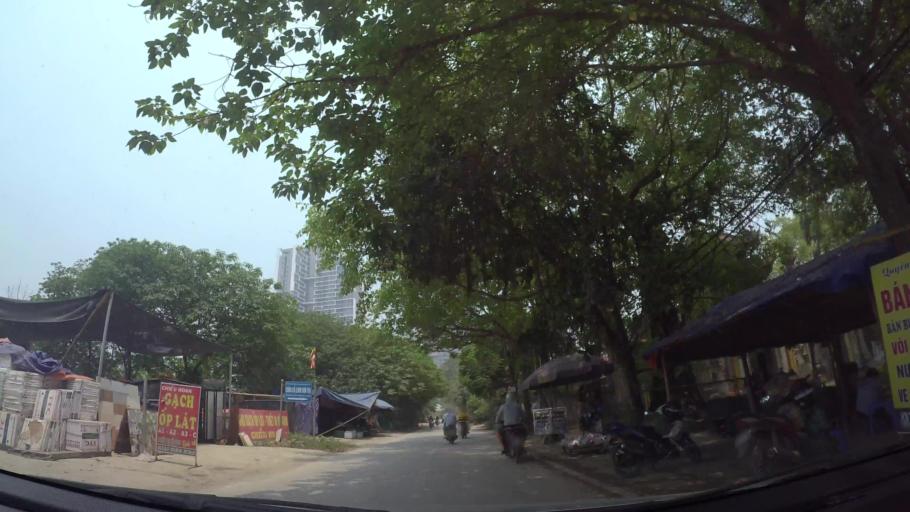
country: VN
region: Ha Noi
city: Thanh Xuan
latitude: 21.0038
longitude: 105.7681
